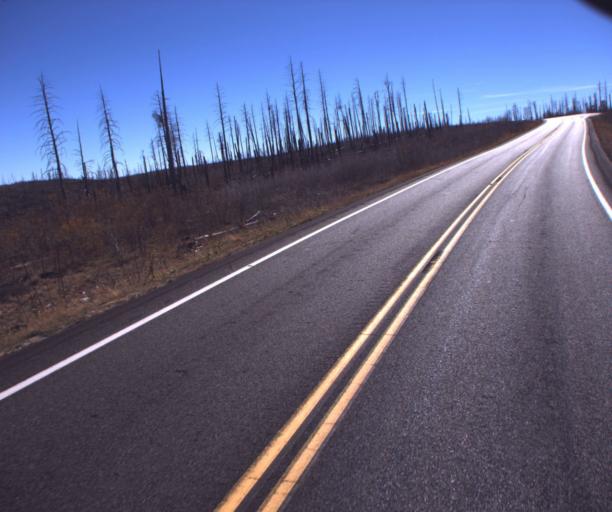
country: US
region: Arizona
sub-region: Coconino County
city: Grand Canyon
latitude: 36.5692
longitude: -112.1732
